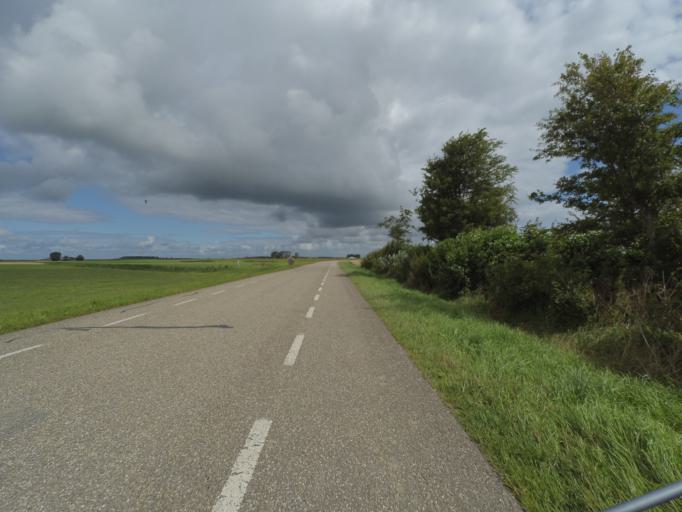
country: NL
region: Groningen
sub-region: Gemeente Zuidhorn
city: Grijpskerk
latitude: 53.3032
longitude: 6.2517
